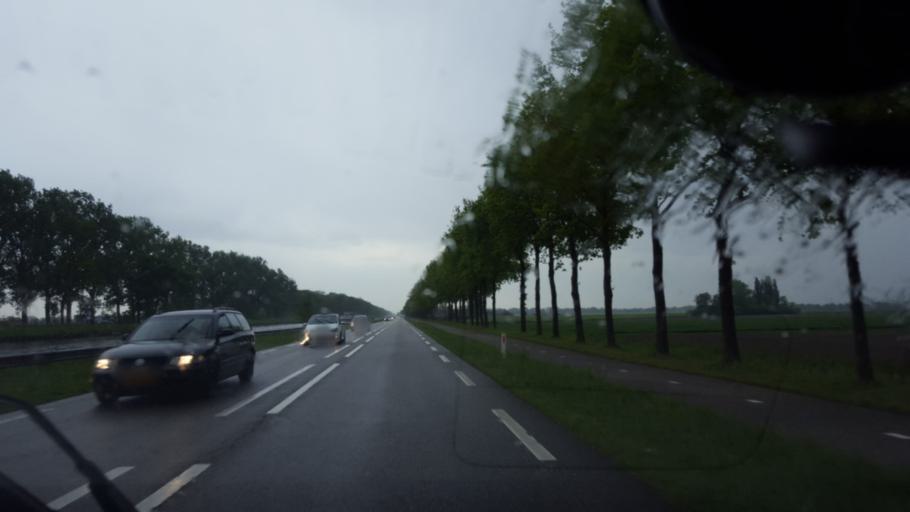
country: NL
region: Limburg
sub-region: Gemeente Nederweert
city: Nederweert
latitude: 51.3261
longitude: 5.7471
